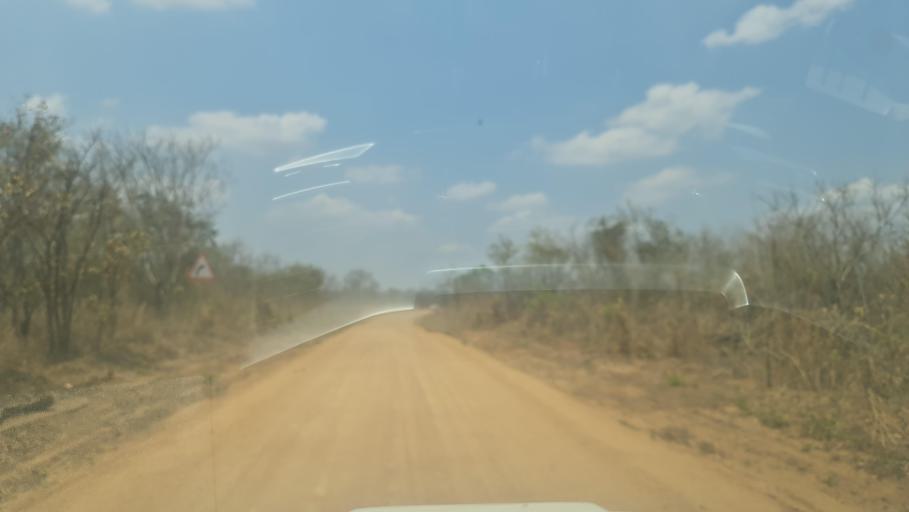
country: MW
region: Southern Region
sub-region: Nsanje District
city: Nsanje
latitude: -17.5725
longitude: 35.9092
